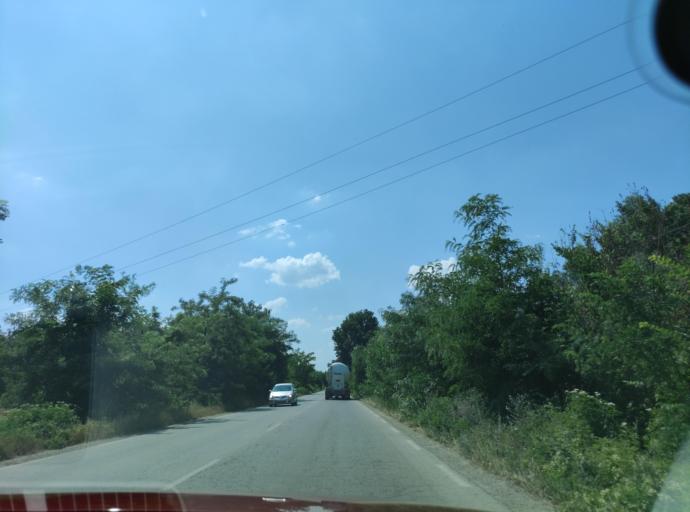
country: BG
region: Pleven
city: Iskur
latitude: 43.4539
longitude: 24.2399
